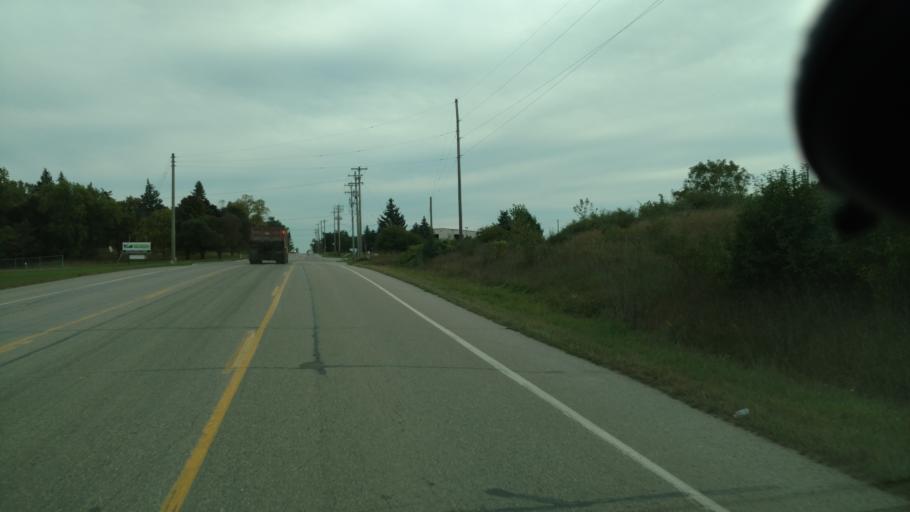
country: US
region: Michigan
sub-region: Ingham County
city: Lansing
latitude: 42.7739
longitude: -84.5231
